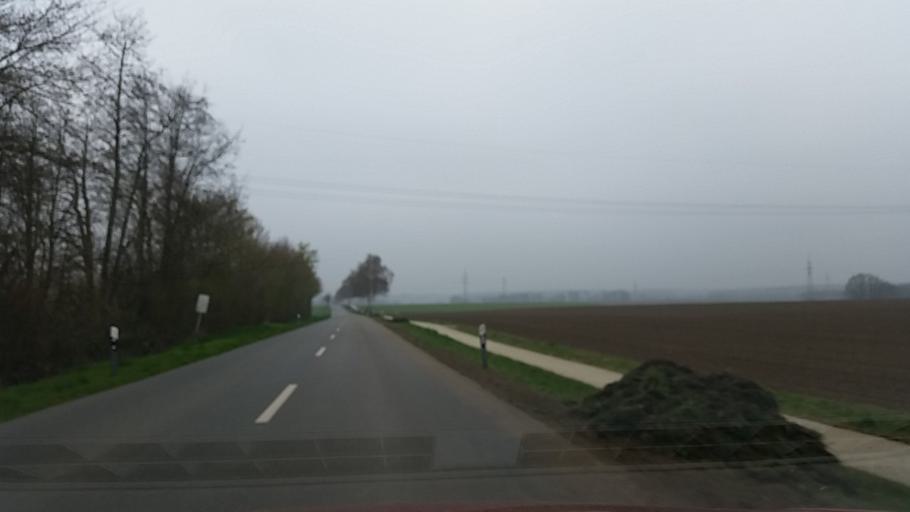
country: DE
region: Lower Saxony
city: Suderburg
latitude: 52.9388
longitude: 10.4852
